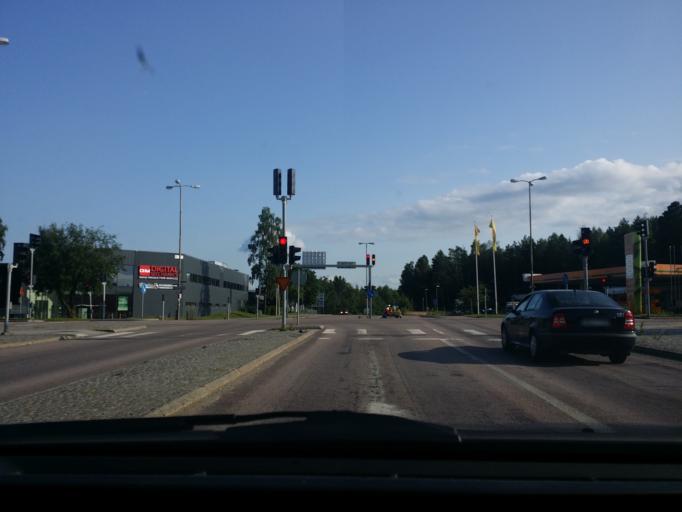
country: SE
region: Vaestmanland
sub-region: Vasteras
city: Vasteras
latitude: 59.6142
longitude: 16.6022
